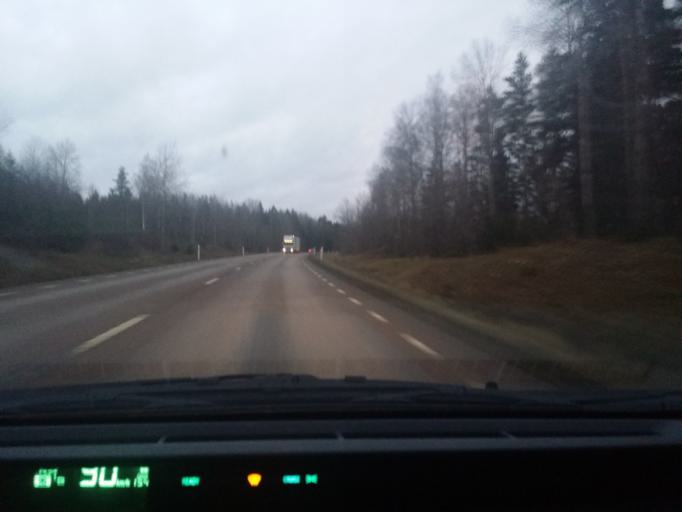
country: SE
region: Soedermanland
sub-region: Eskilstuna Kommun
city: Kvicksund
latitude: 59.5024
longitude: 16.3041
